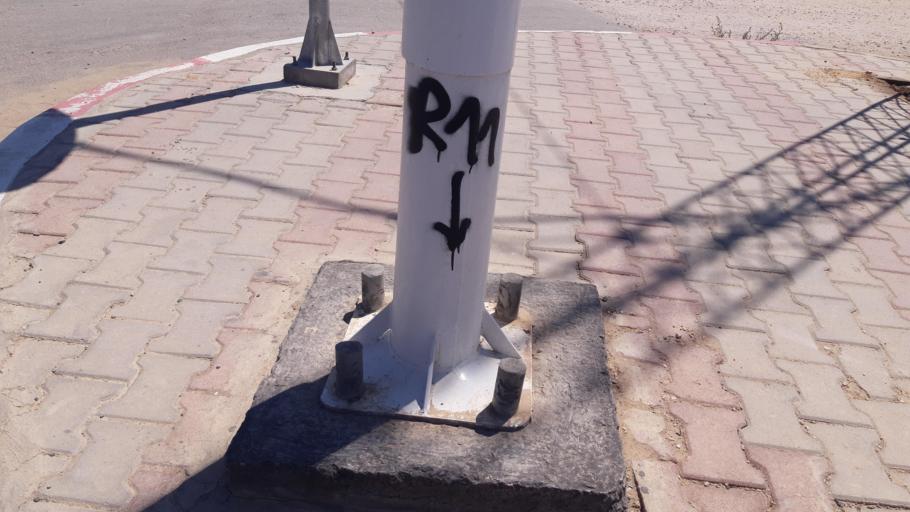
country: TN
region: Safaqis
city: Sfax
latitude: 34.7294
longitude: 10.7257
